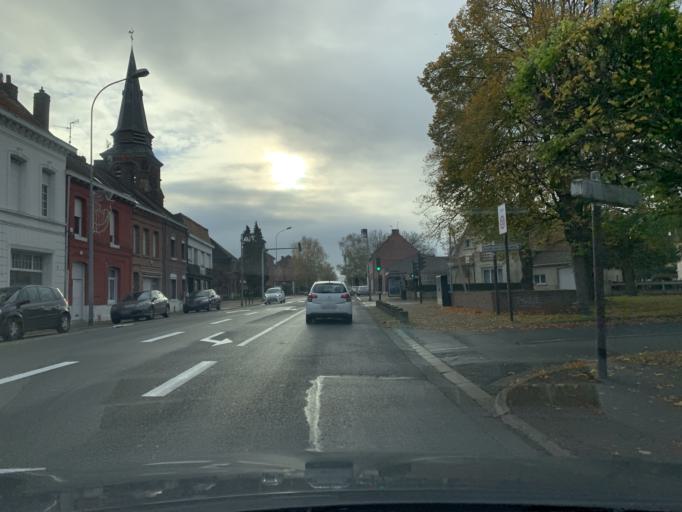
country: FR
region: Nord-Pas-de-Calais
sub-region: Departement du Nord
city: Lambres-lez-Douai
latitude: 50.3537
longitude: 3.0846
